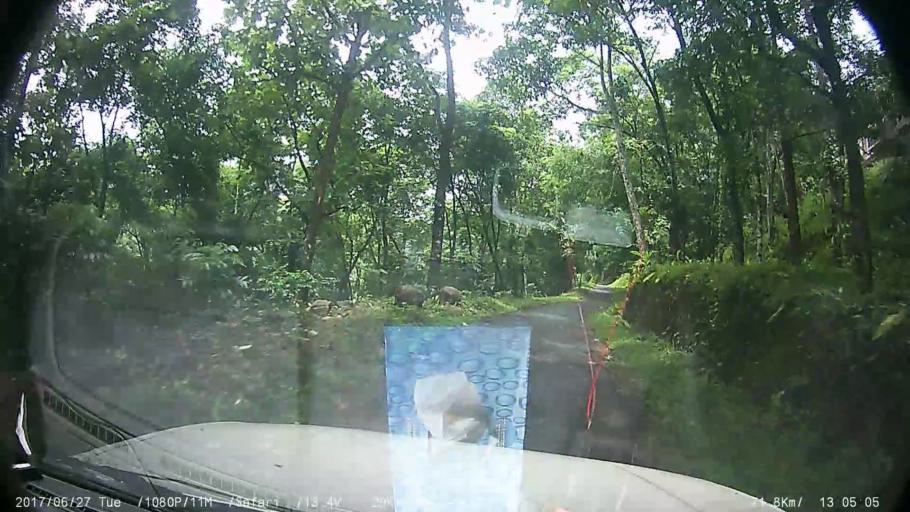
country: IN
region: Kerala
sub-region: Kottayam
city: Palackattumala
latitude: 9.7851
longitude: 76.5478
